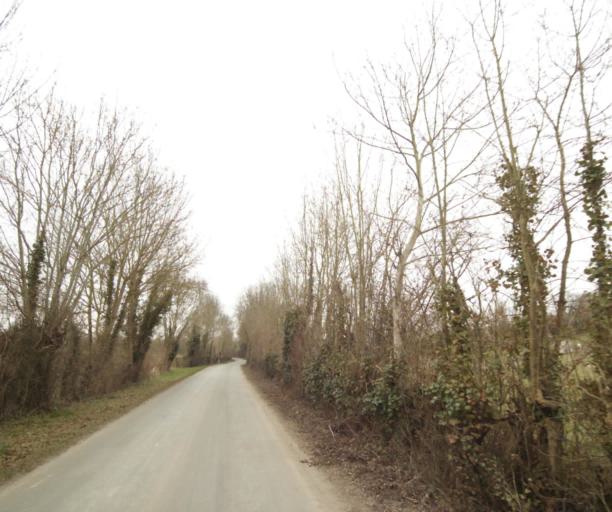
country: FR
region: Poitou-Charentes
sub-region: Departement des Deux-Sevres
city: Magne
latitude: 46.3261
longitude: -0.5292
